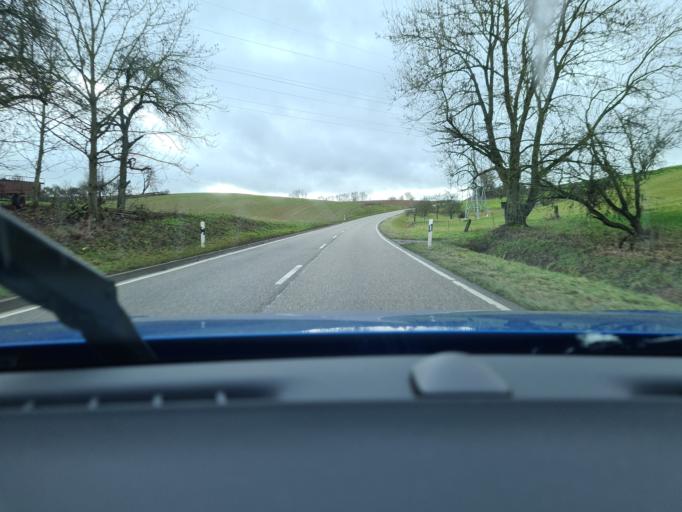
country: DE
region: Baden-Wuerttemberg
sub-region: Karlsruhe Region
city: Mauer
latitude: 49.3274
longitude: 8.7895
